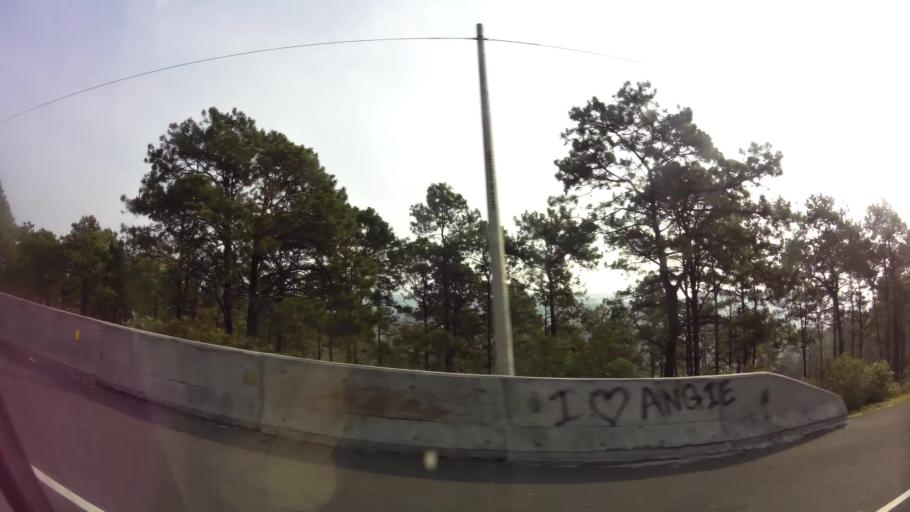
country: HN
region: Francisco Morazan
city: Zambrano
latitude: 14.2522
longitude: -87.3818
